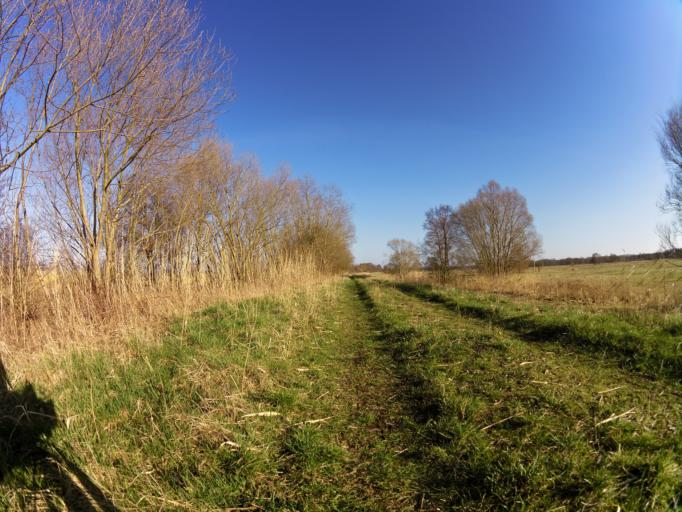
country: PL
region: West Pomeranian Voivodeship
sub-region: Powiat policki
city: Nowe Warpno
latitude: 53.6984
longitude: 14.3692
